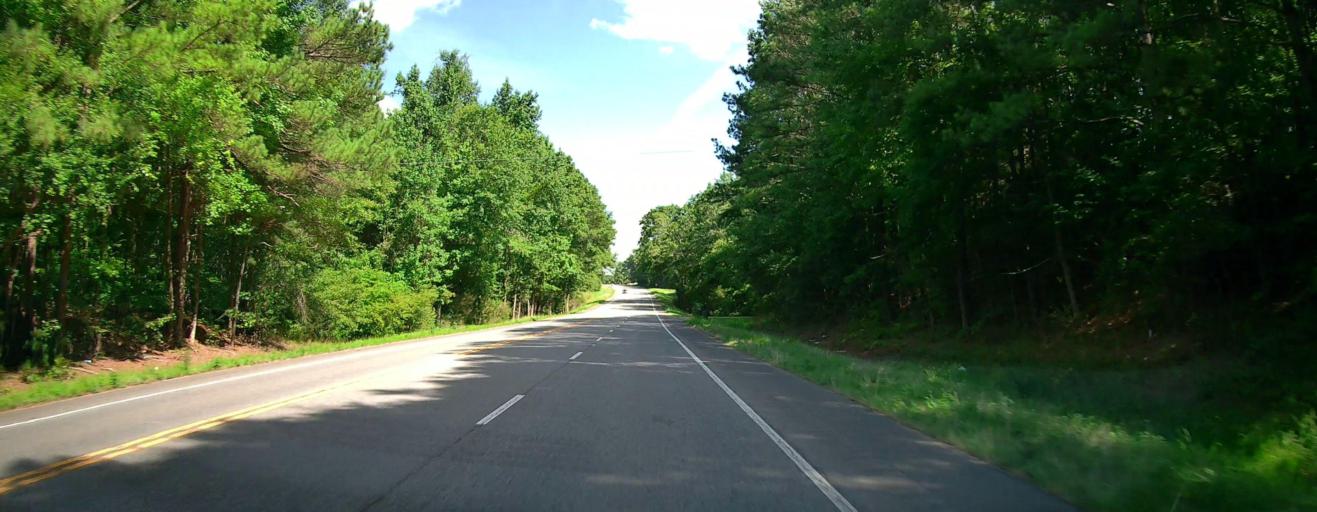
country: US
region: Alabama
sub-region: Pickens County
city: Gordo
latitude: 33.2944
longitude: -87.8746
